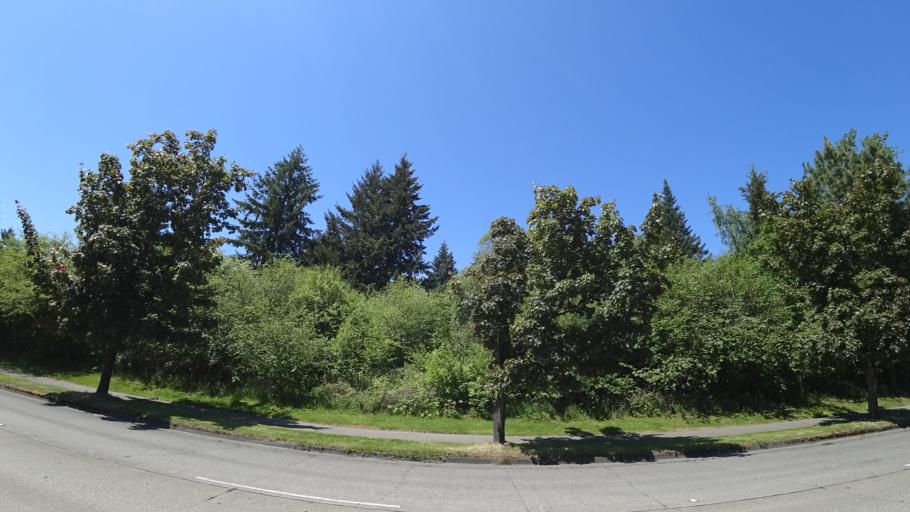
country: US
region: Oregon
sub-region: Washington County
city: Aloha
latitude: 45.4949
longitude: -122.8398
